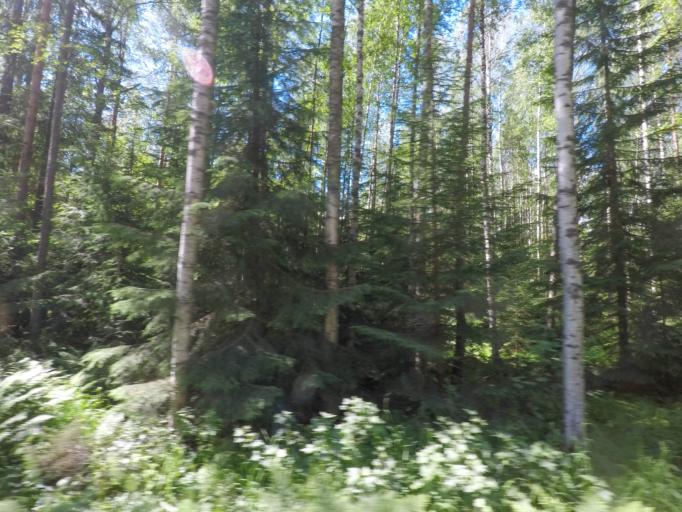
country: FI
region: Central Finland
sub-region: Jyvaeskylae
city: Hankasalmi
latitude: 62.4365
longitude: 26.6467
